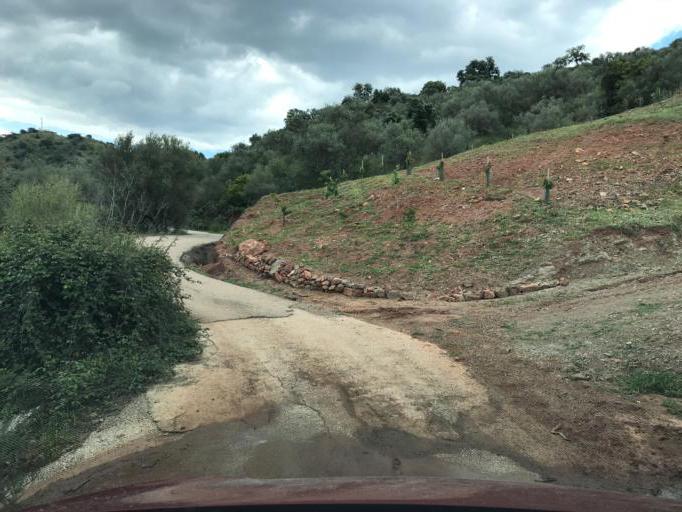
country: ES
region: Andalusia
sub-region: Provincia de Malaga
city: Comares
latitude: 36.8774
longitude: -4.2601
